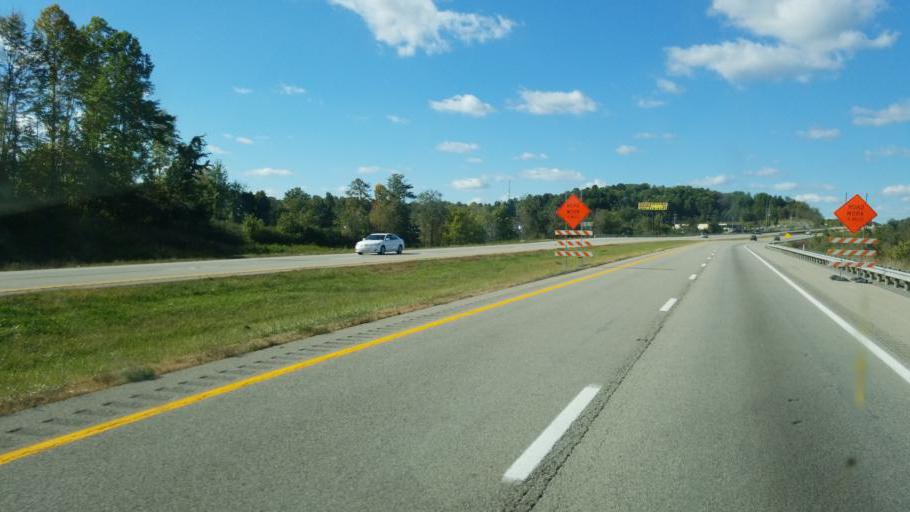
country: US
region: West Virginia
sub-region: Monongalia County
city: Star City
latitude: 39.6891
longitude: -80.0405
